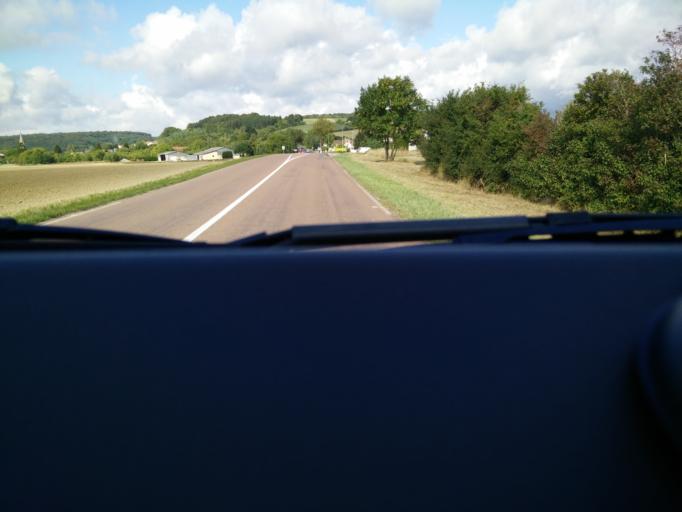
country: FR
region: Lorraine
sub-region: Departement de la Meuse
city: Etain
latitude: 49.1173
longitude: 5.5696
